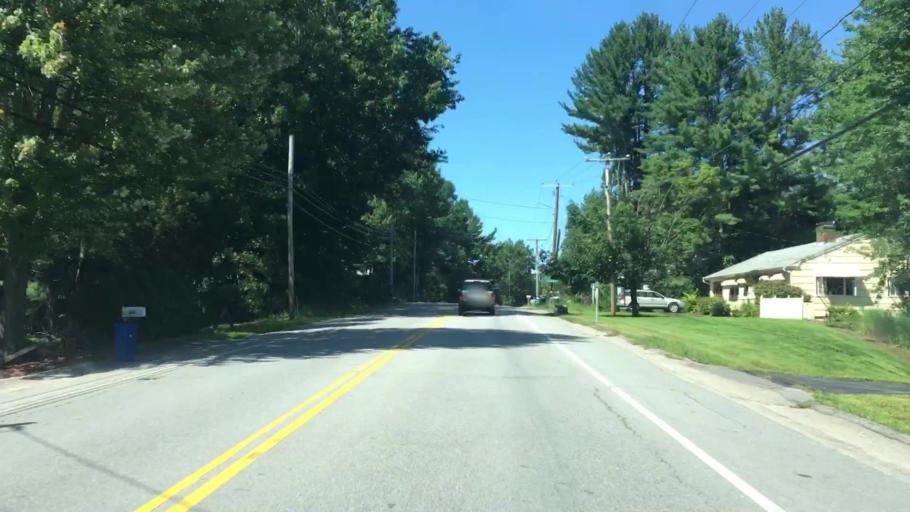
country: US
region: Maine
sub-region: York County
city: Eliot
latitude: 43.1397
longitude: -70.8380
